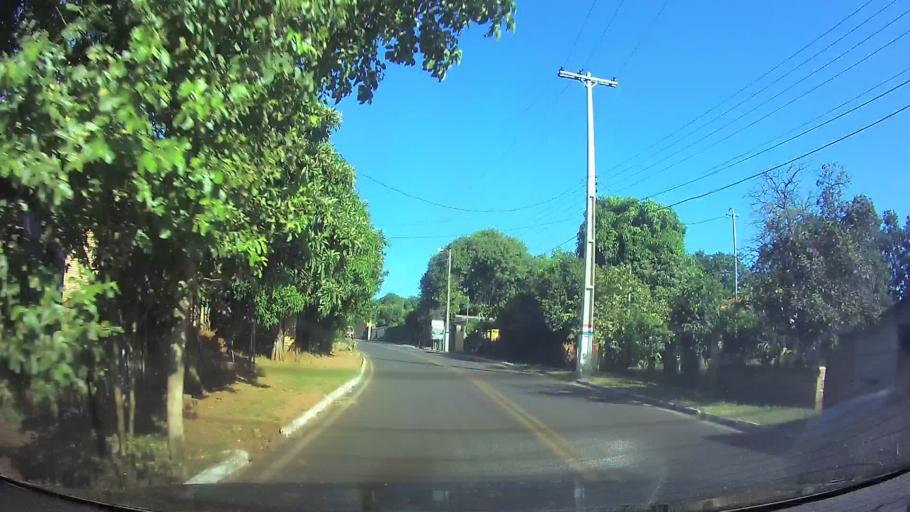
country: PY
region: Cordillera
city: Atyra
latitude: -25.2841
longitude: -57.1724
